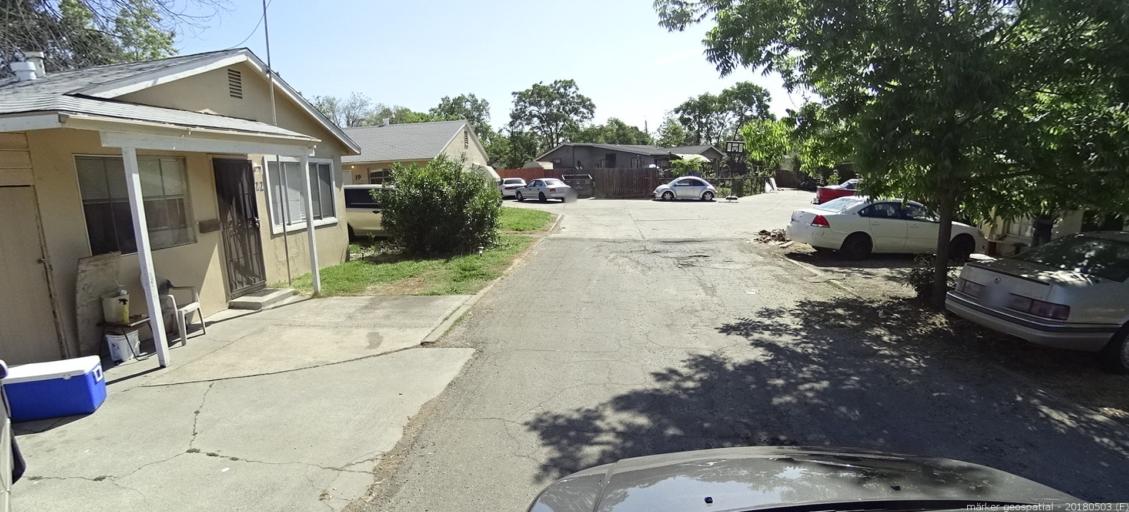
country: US
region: California
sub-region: Sacramento County
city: Arden-Arcade
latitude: 38.6208
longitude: -121.4391
